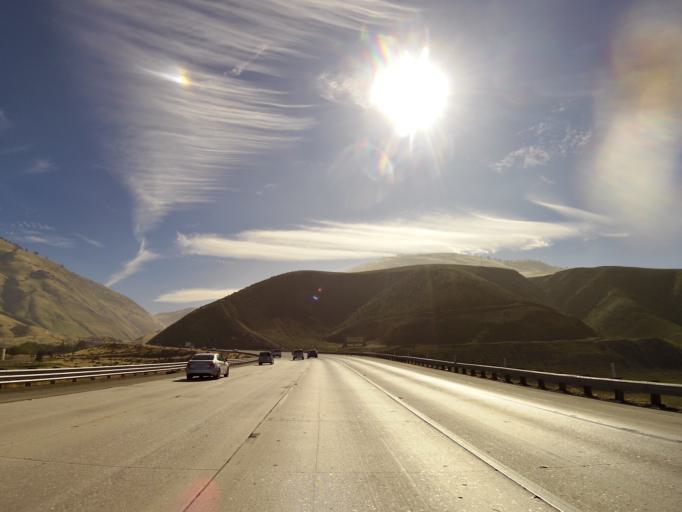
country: US
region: California
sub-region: Kern County
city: Frazier Park
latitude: 34.9340
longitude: -118.9310
